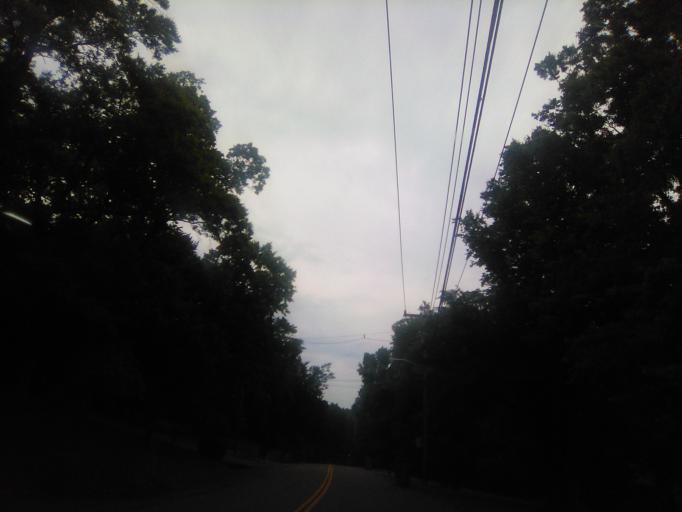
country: US
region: Tennessee
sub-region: Davidson County
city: Belle Meade
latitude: 36.1065
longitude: -86.8955
